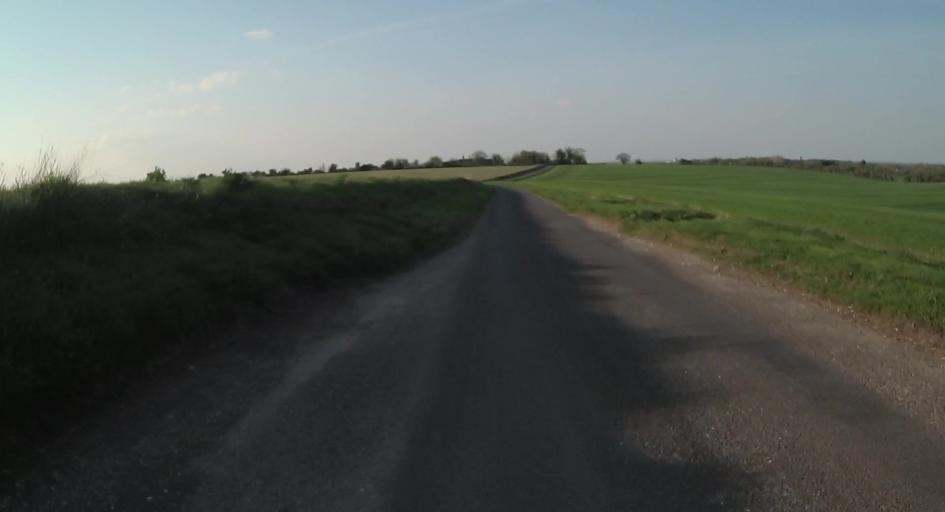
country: GB
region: England
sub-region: Hampshire
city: Basingstoke
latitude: 51.2261
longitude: -1.0910
